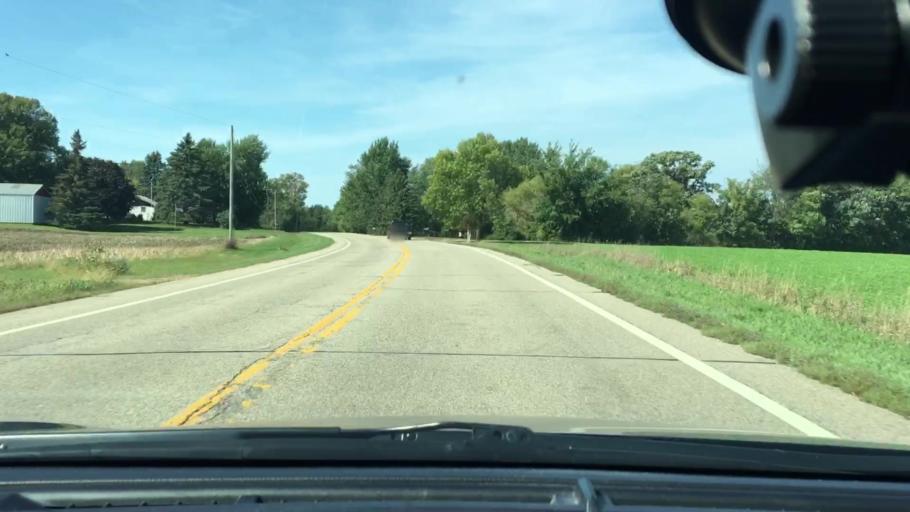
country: US
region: Minnesota
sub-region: Wright County
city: Hanover
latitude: 45.1224
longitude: -93.6128
